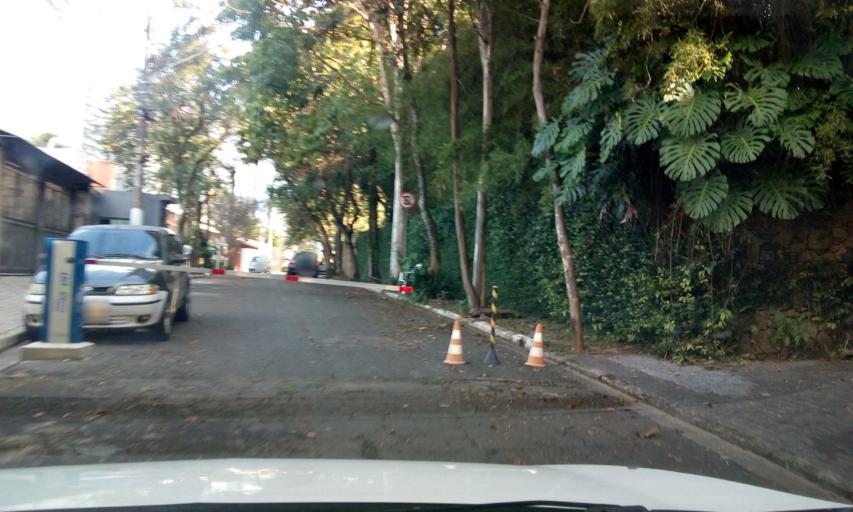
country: BR
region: Sao Paulo
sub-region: Taboao Da Serra
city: Taboao da Serra
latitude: -23.6202
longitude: -46.7050
